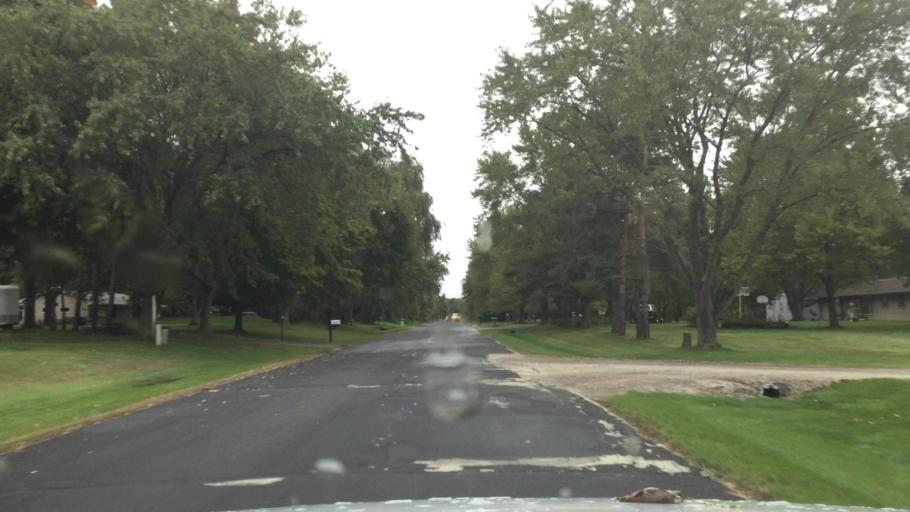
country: US
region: Wisconsin
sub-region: Racine County
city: Waterford
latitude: 42.7588
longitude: -88.1850
